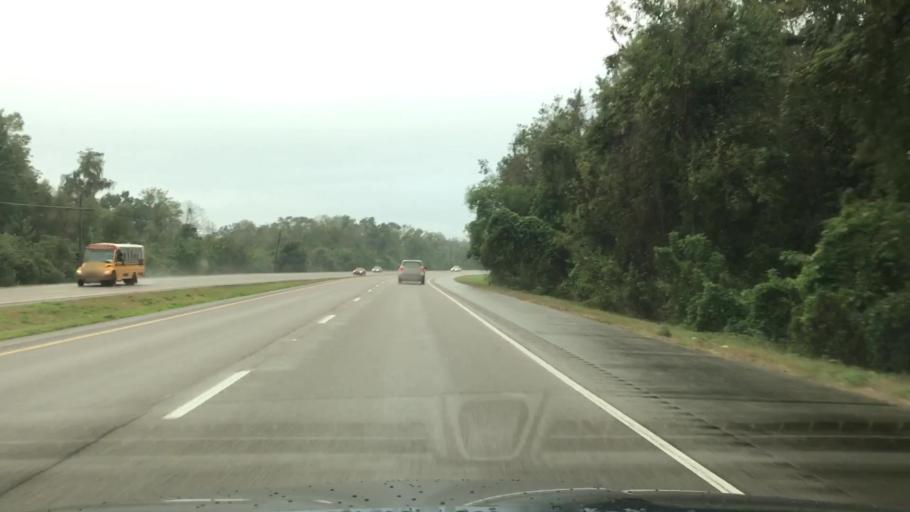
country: US
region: Louisiana
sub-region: Saint Charles Parish
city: Des Allemands
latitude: 29.8458
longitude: -90.4480
